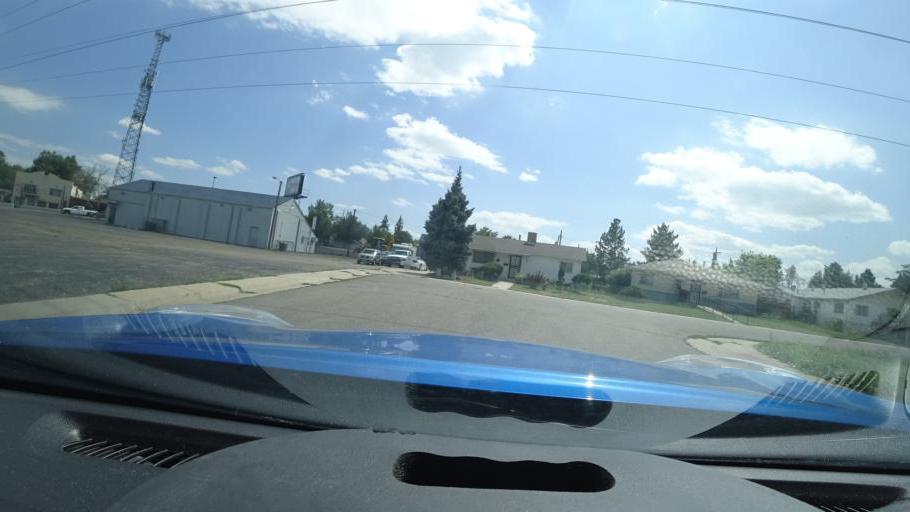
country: US
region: Colorado
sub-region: Jefferson County
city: Lakewood
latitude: 39.7016
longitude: -105.0479
